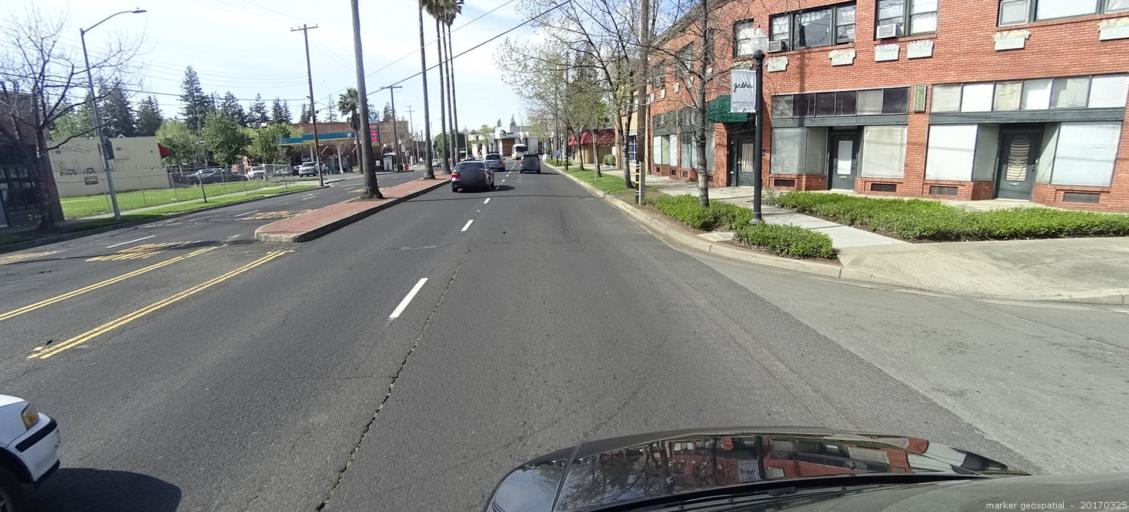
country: US
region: California
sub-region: Sacramento County
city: Sacramento
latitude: 38.5552
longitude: -121.4715
